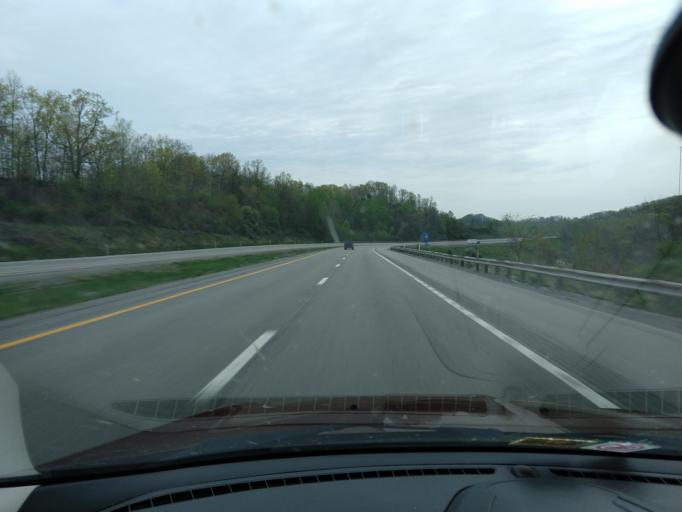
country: US
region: West Virginia
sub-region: Lewis County
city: Weston
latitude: 38.9512
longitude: -80.5344
